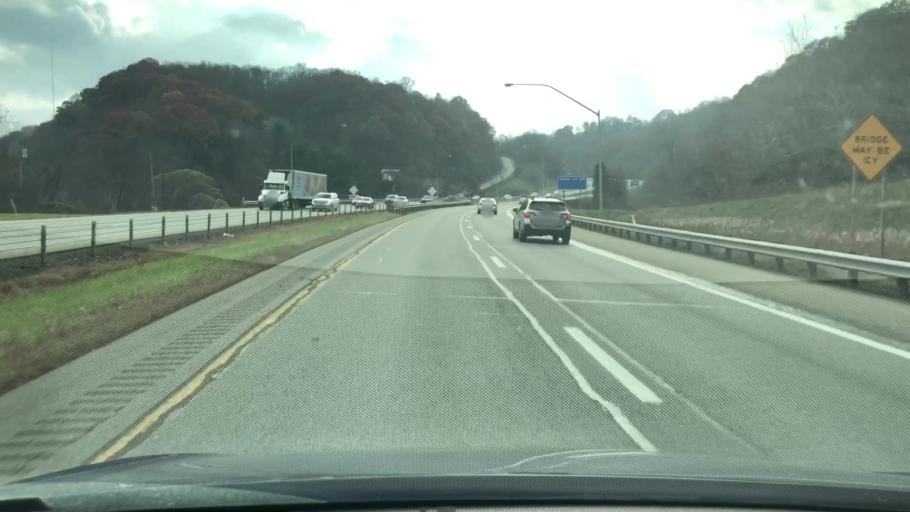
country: US
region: Pennsylvania
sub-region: Westmoreland County
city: Arnold
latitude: 40.5839
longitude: -79.7796
